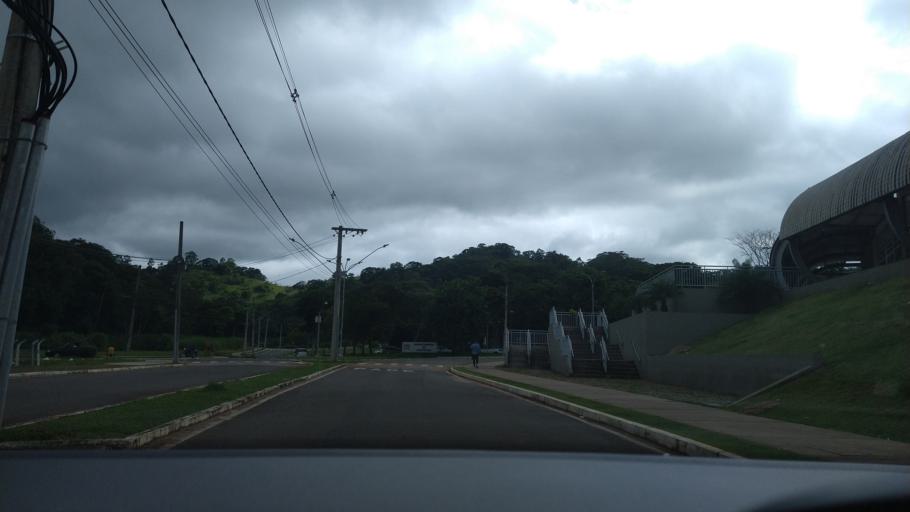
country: BR
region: Minas Gerais
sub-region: Vicosa
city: Vicosa
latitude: -20.7674
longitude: -42.8616
